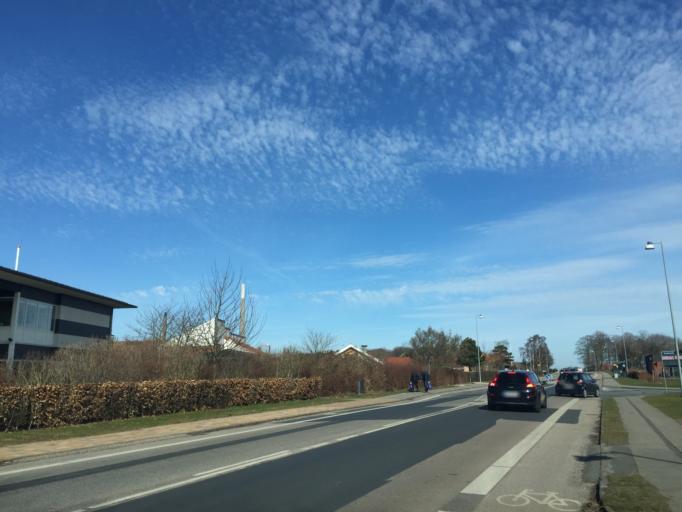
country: DK
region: South Denmark
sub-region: Odense Kommune
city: Stige
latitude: 55.4181
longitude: 10.4021
